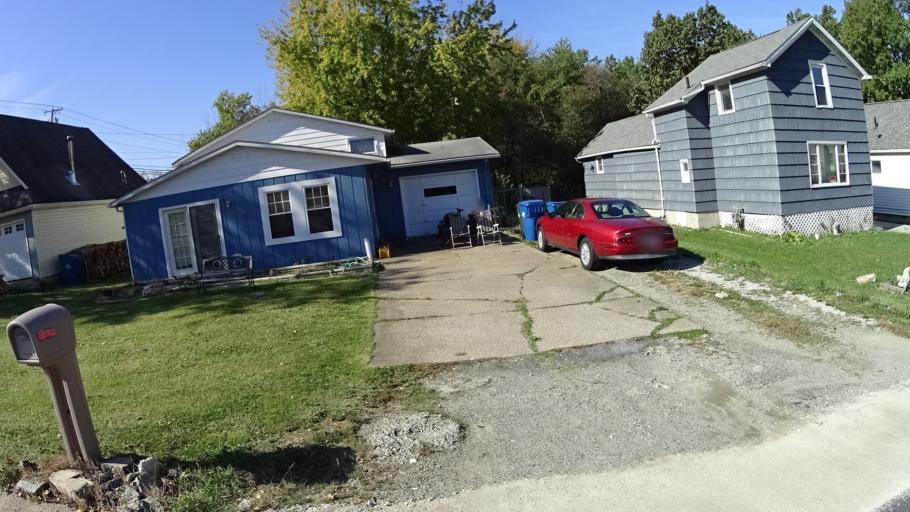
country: US
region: Ohio
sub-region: Lorain County
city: Vermilion-on-the-Lake
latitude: 41.4253
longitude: -82.3103
